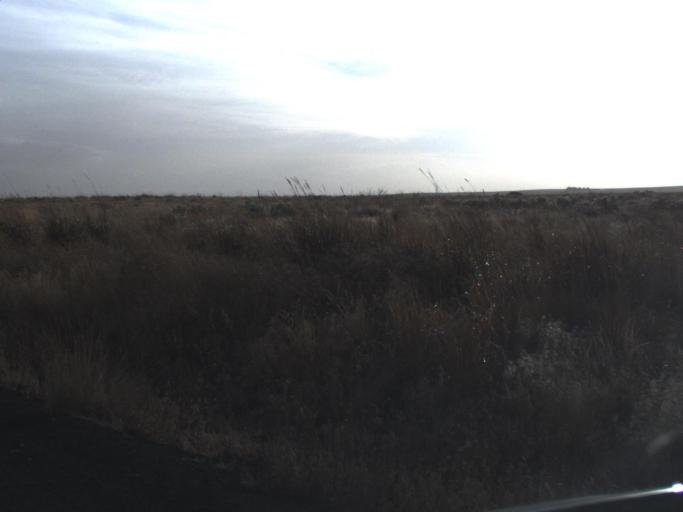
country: US
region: Washington
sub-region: Adams County
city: Ritzville
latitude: 47.3100
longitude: -118.6904
